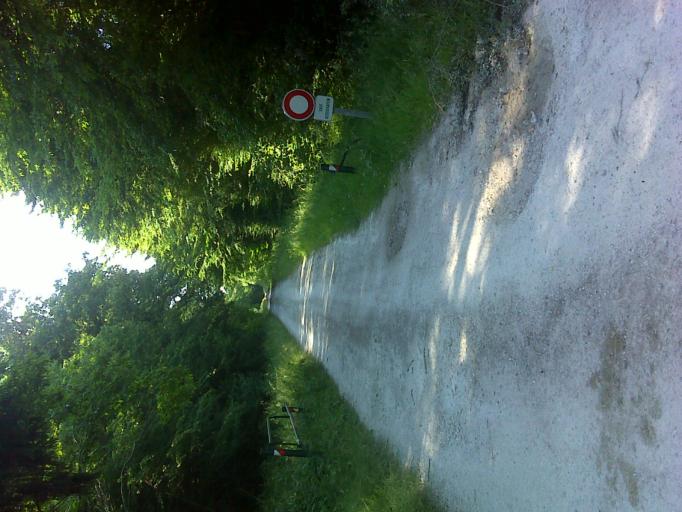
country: FR
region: Champagne-Ardenne
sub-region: Departement de la Haute-Marne
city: Laneuville-a-Remy
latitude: 48.5578
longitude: 4.8397
